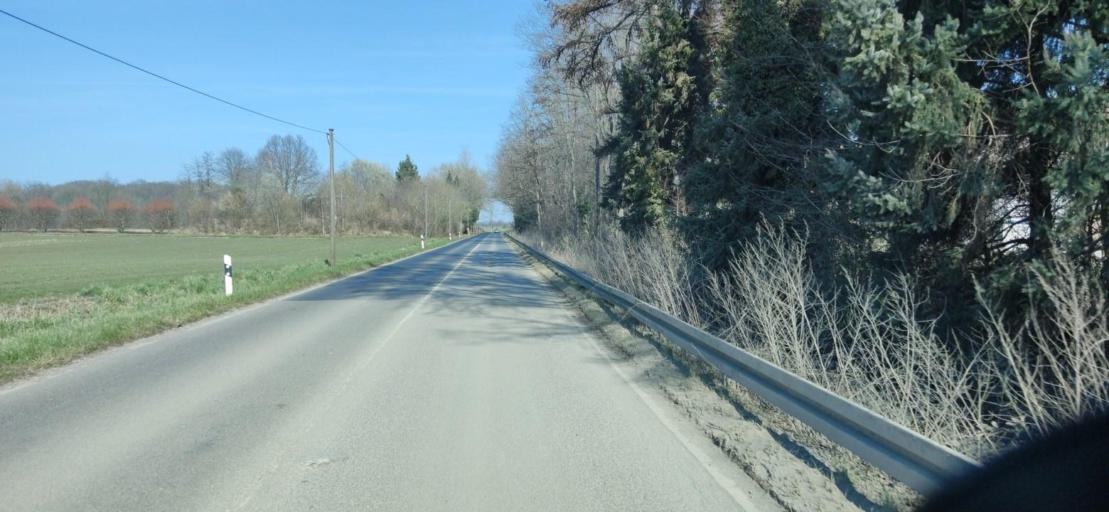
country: DE
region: North Rhine-Westphalia
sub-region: Regierungsbezirk Dusseldorf
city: Erkrath
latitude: 51.2426
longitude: 6.8918
